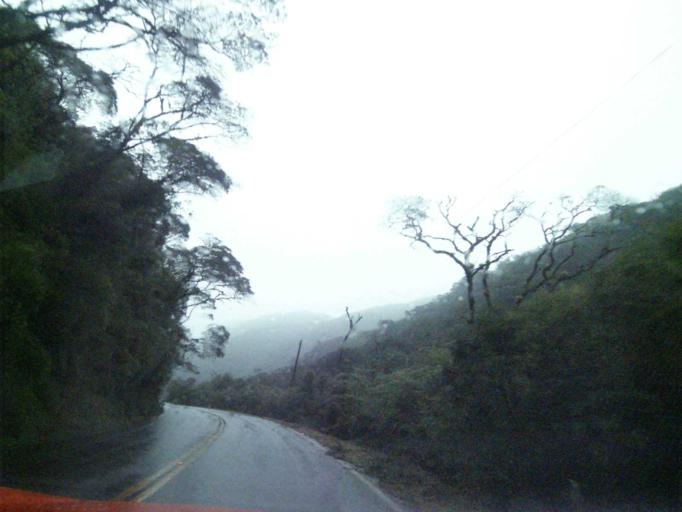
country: BR
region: Santa Catarina
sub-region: Anitapolis
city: Anitapolis
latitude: -27.7605
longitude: -49.0378
